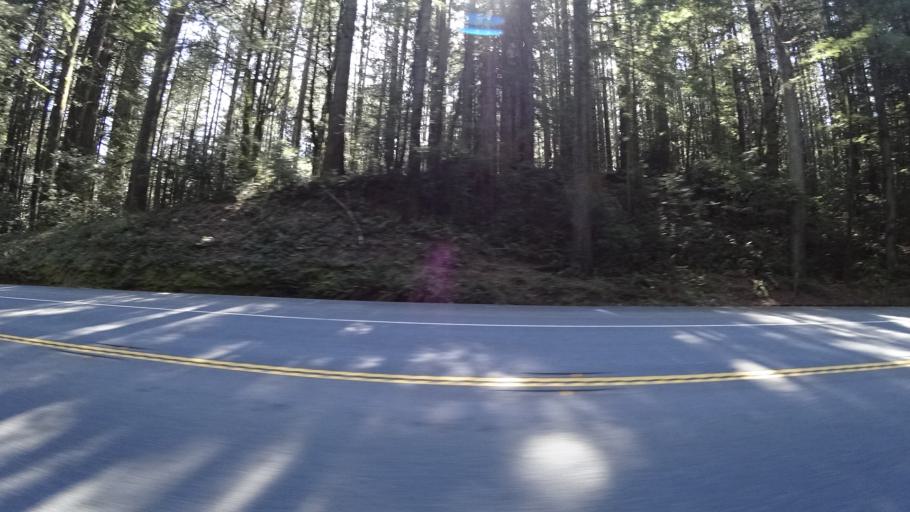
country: US
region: California
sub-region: Del Norte County
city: Bertsch-Oceanview
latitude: 41.6859
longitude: -124.1067
